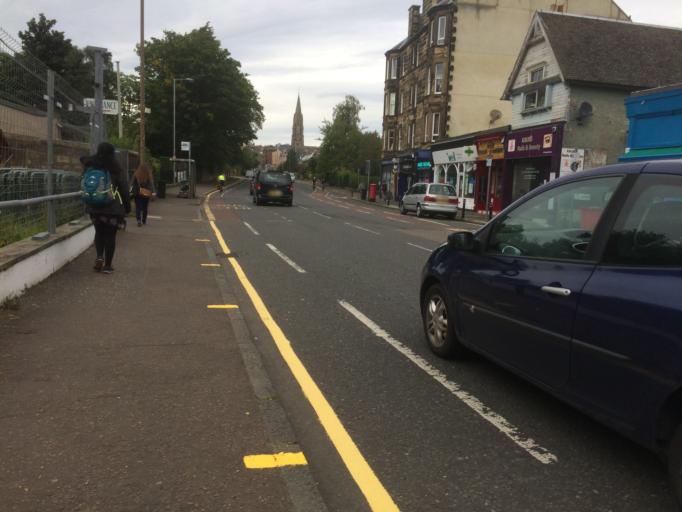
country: GB
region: Scotland
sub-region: Edinburgh
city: Edinburgh
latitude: 55.9301
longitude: -3.1761
